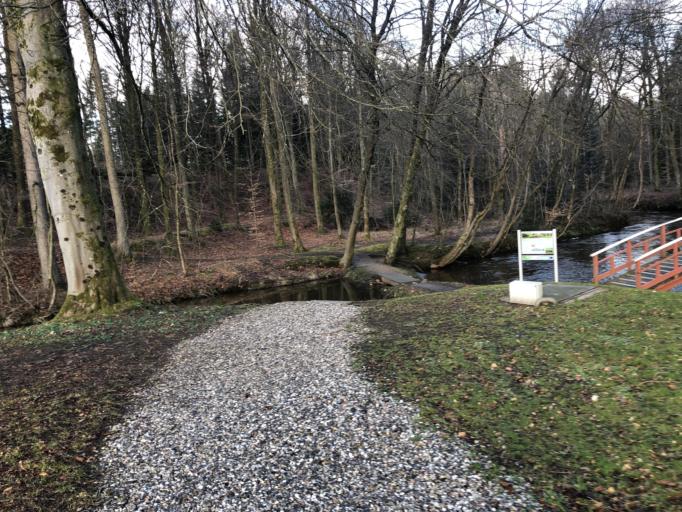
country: DK
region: Central Jutland
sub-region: Herning Kommune
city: Kibaek
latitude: 55.9502
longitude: 8.8797
